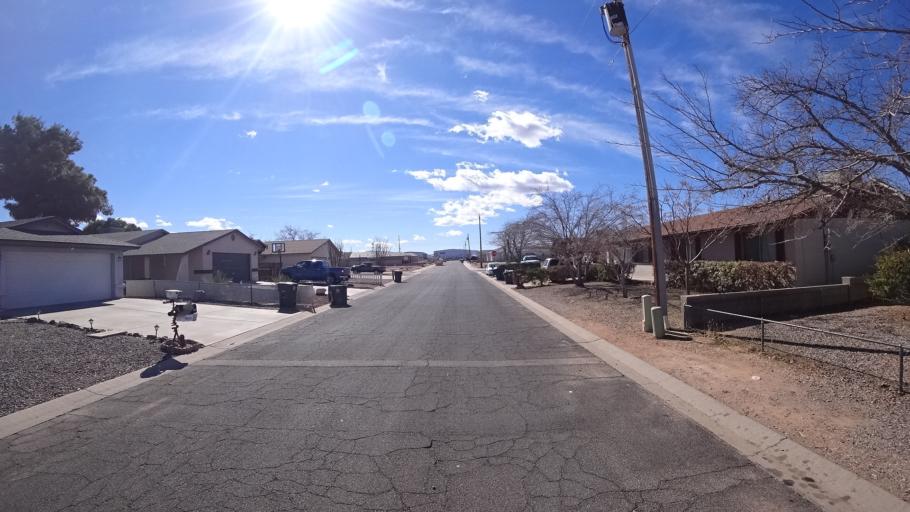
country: US
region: Arizona
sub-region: Mohave County
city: New Kingman-Butler
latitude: 35.2274
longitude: -114.0192
